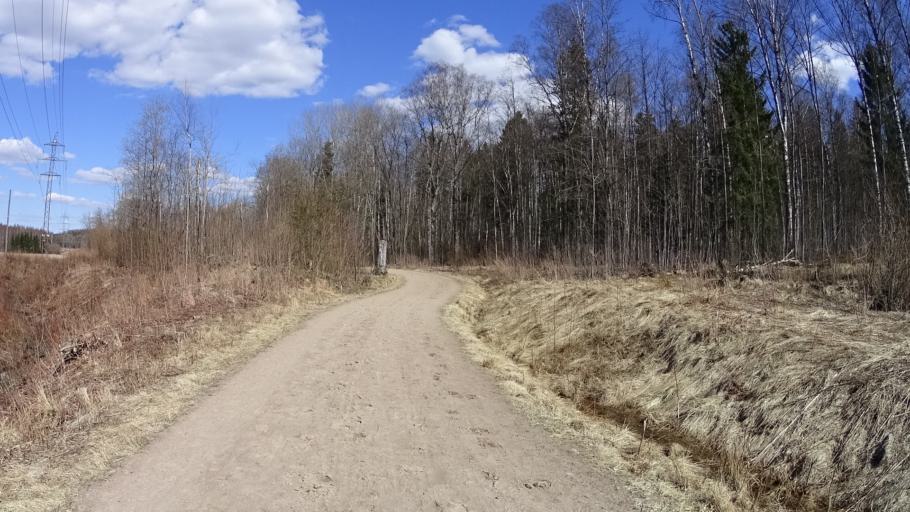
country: FI
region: Uusimaa
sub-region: Helsinki
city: Kilo
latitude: 60.2346
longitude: 24.7885
